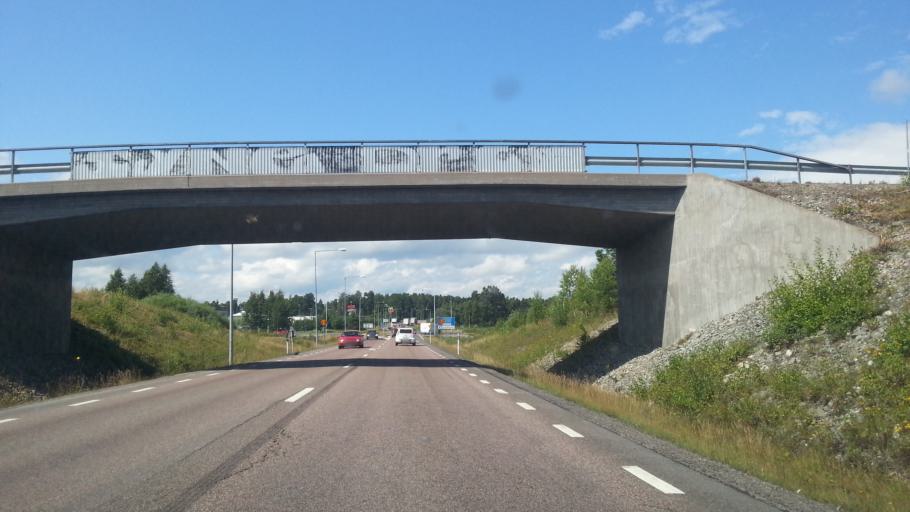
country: SE
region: Dalarna
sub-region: Faluns Kommun
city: Falun
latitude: 60.6066
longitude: 15.6640
